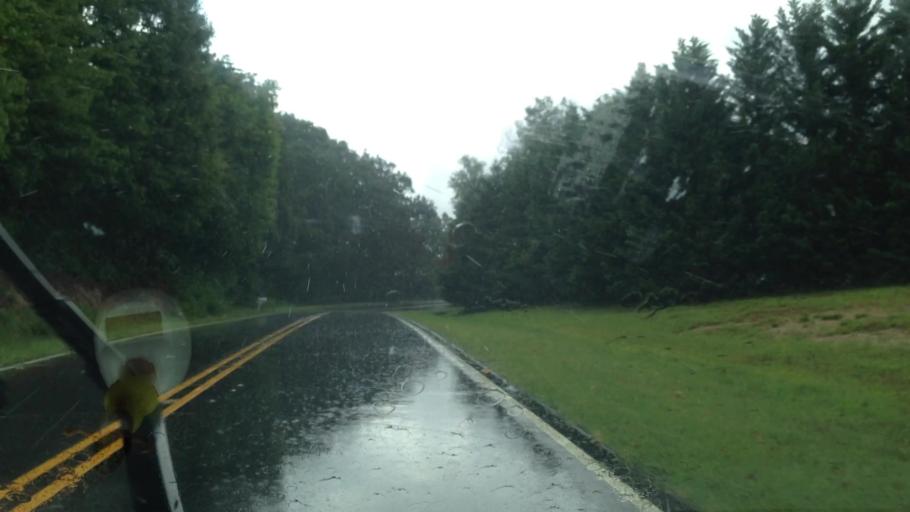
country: US
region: North Carolina
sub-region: Stokes County
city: Danbury
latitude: 36.4291
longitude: -80.0938
